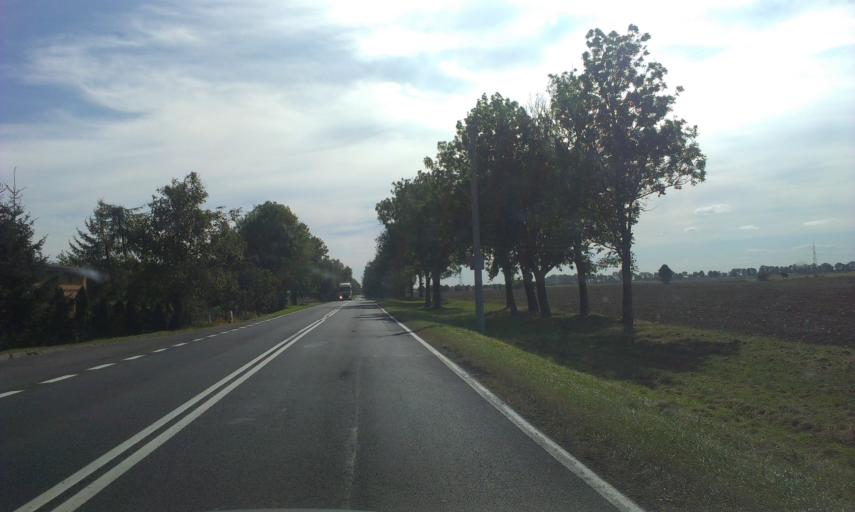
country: PL
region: Greater Poland Voivodeship
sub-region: Powiat zlotowski
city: Okonek
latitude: 53.6184
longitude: 16.7852
